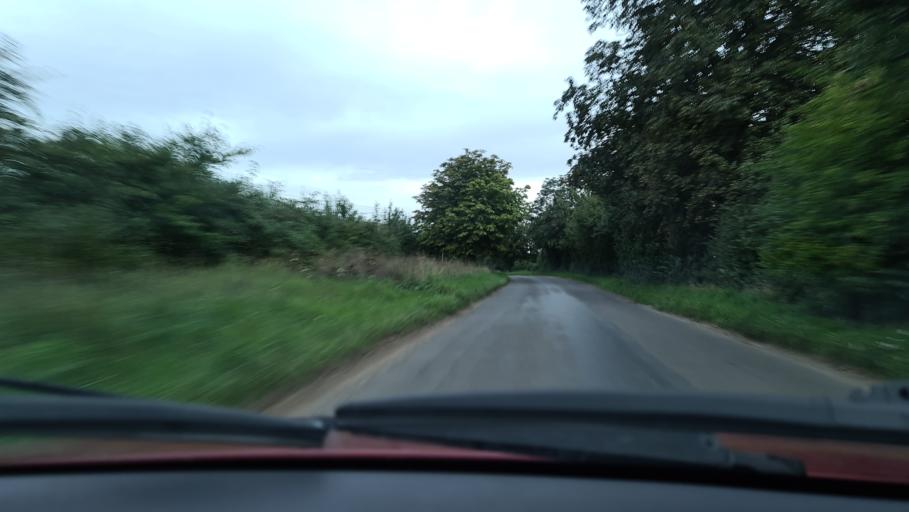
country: GB
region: England
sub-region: Oxfordshire
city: Deddington
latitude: 51.9560
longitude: -1.3125
